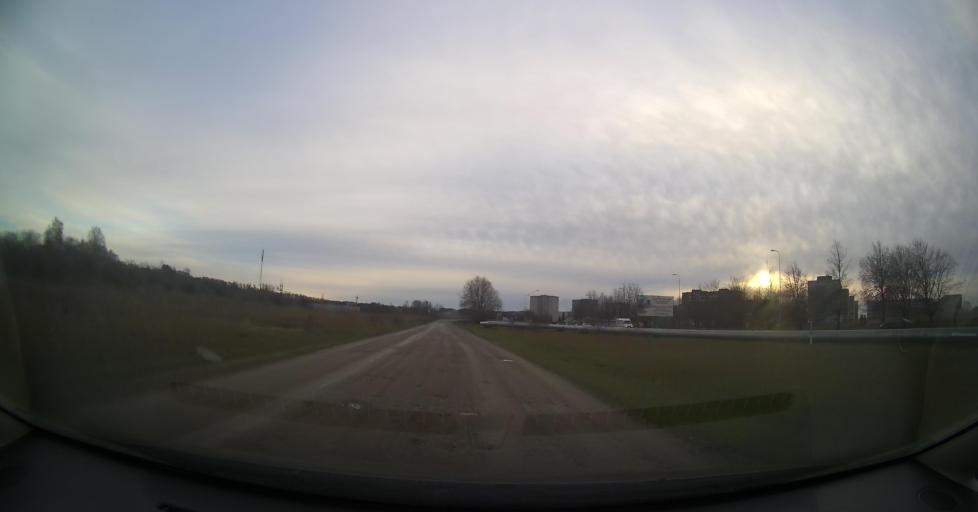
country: EE
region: Ida-Virumaa
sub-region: Johvi vald
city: Johvi
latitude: 59.3414
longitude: 27.4206
